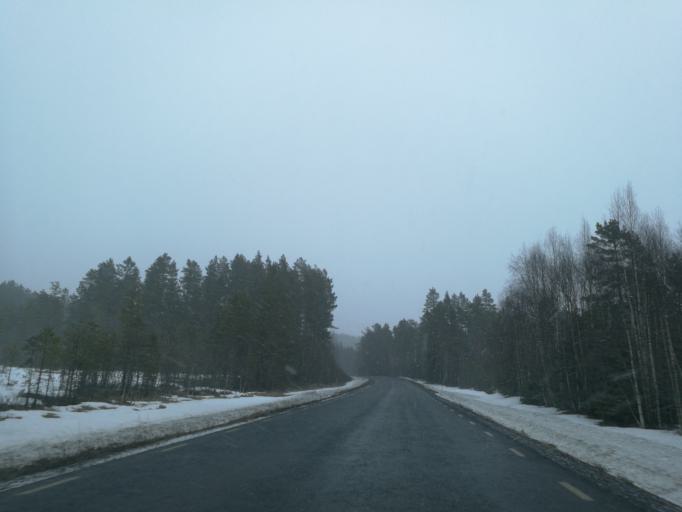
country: NO
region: Hedmark
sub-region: Grue
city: Kirkenaer
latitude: 60.6798
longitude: 12.6603
